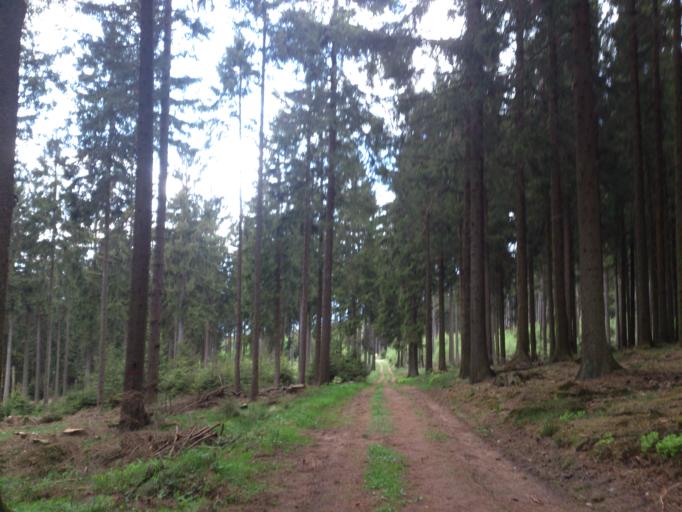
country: DE
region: North Rhine-Westphalia
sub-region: Regierungsbezirk Detmold
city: Willebadessen
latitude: 51.5972
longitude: 9.0122
